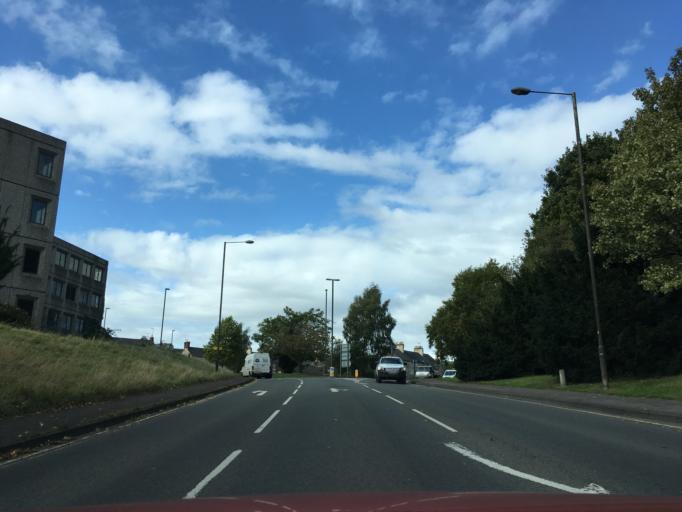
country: GB
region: England
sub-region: Gloucestershire
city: Stroud
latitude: 51.7429
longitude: -2.2394
